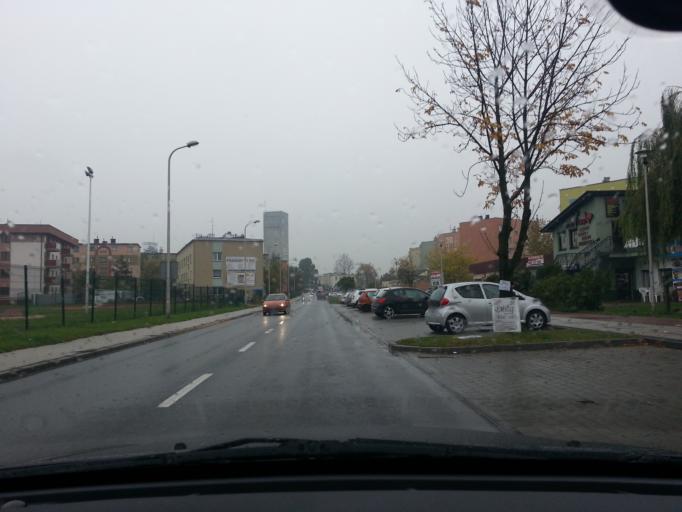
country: PL
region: Silesian Voivodeship
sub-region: Powiat gliwicki
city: Knurow
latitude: 50.2304
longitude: 18.6571
